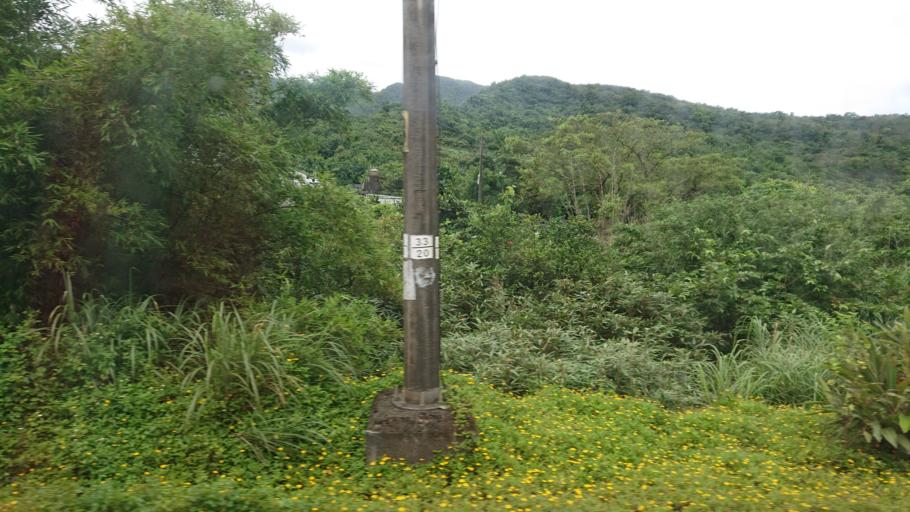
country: TW
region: Taiwan
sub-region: Keelung
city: Keelung
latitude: 25.0070
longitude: 121.9565
